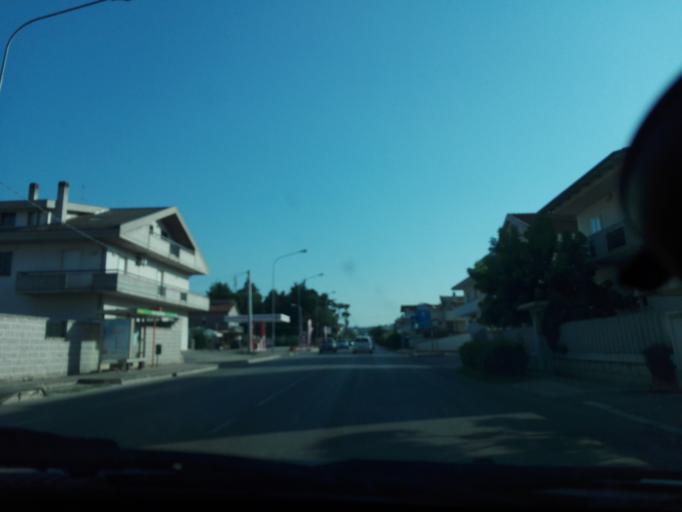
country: IT
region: Abruzzo
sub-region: Provincia di Pescara
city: Cappelle sul Tavo
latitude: 42.4888
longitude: 14.1212
